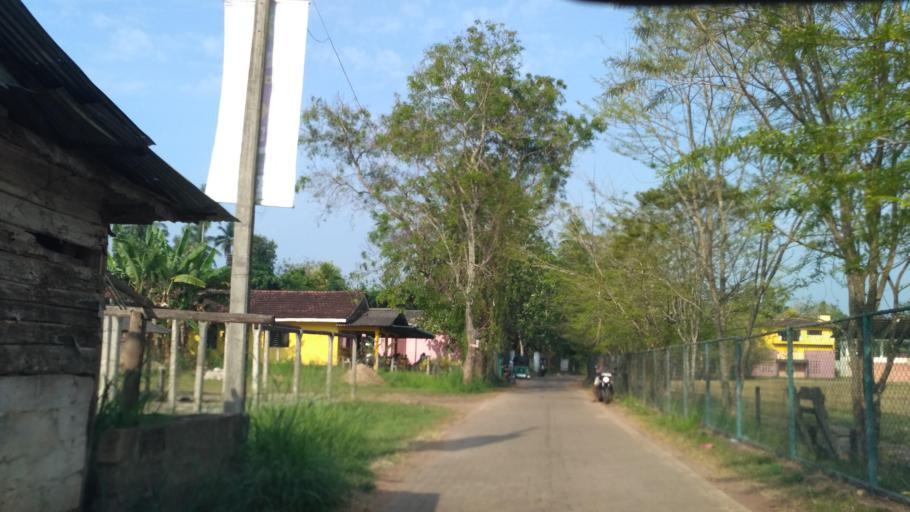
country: LK
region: North Western
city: Kuliyapitiya
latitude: 7.3270
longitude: 80.0237
